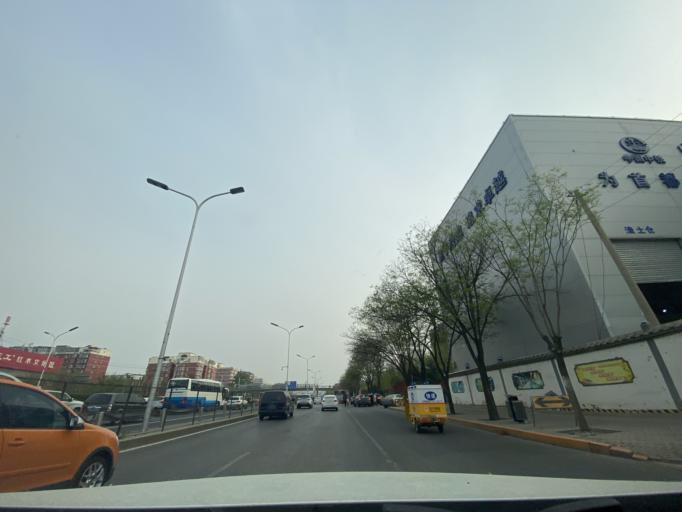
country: CN
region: Beijing
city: Sijiqing
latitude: 39.9367
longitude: 116.2679
